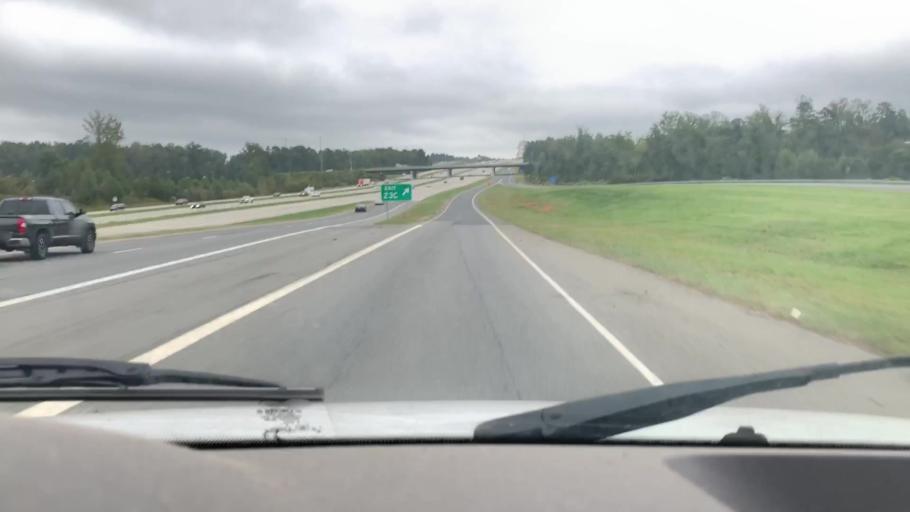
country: US
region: North Carolina
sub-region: Mecklenburg County
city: Huntersville
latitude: 35.3642
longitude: -80.8338
